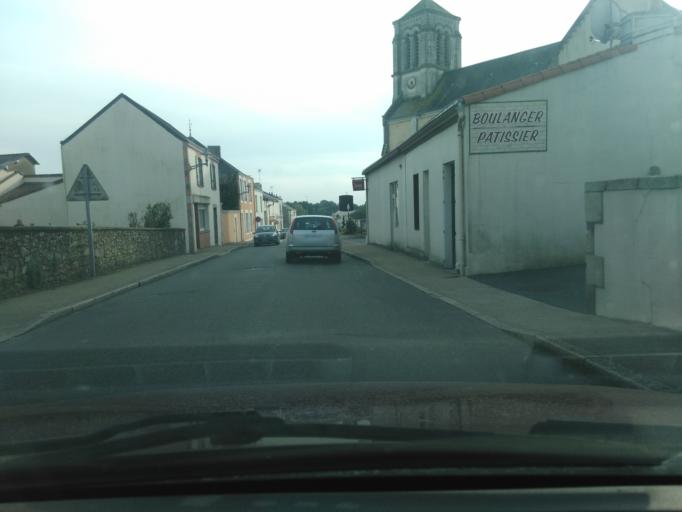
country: FR
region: Pays de la Loire
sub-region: Departement de la Vendee
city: Dompierre-sur-Yon
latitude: 46.7392
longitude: -1.3845
